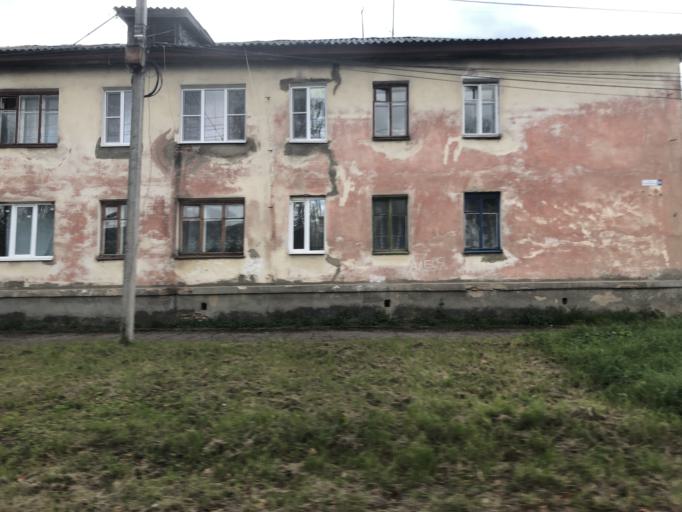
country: RU
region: Tverskaya
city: Rzhev
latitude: 56.2544
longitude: 34.2930
